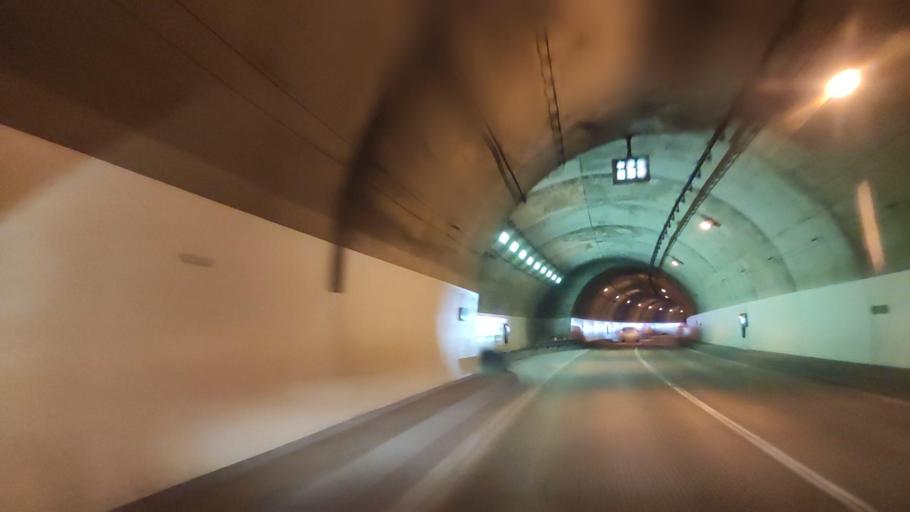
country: JP
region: Hokkaido
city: Ishikari
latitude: 43.4547
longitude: 141.4093
